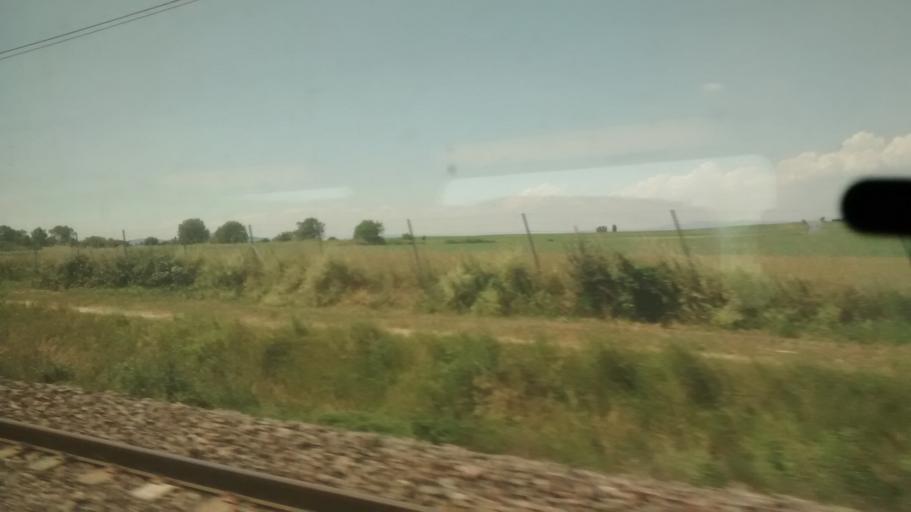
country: FR
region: Rhone-Alpes
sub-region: Departement de l'Ain
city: Civrieux
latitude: 45.9505
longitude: 4.8658
